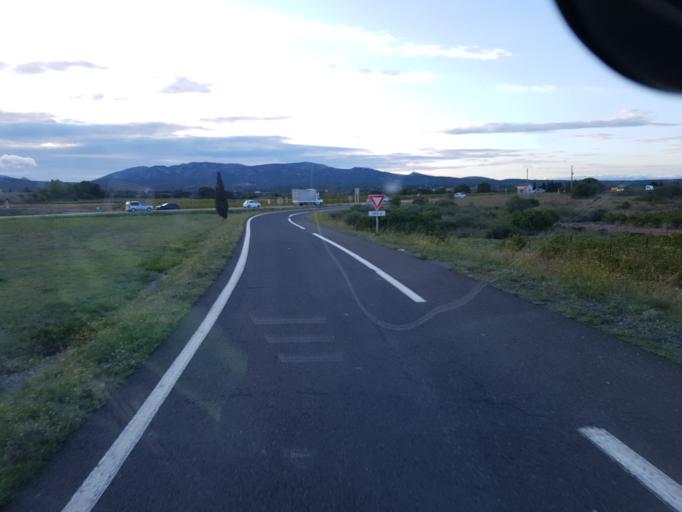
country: FR
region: Languedoc-Roussillon
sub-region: Departement de l'Aude
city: Leucate
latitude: 42.9375
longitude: 2.9922
